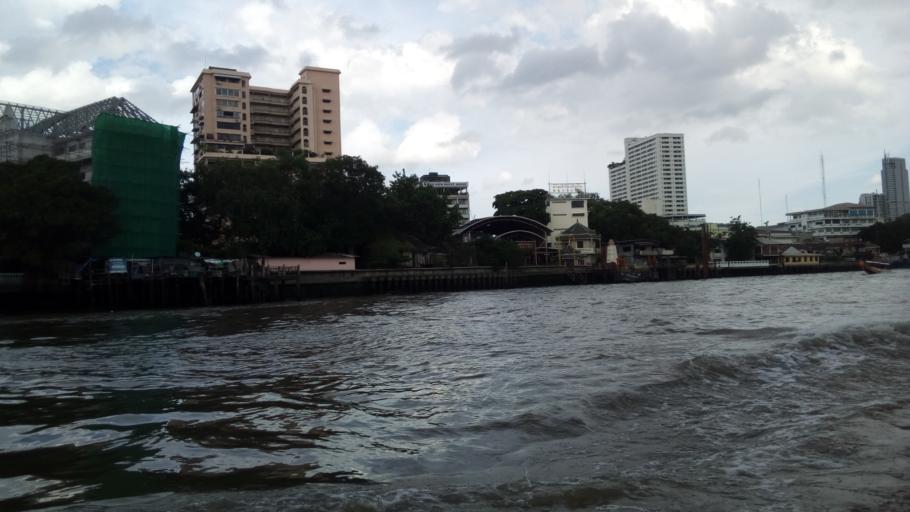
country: TH
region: Bangkok
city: Khlong San
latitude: 13.7349
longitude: 100.5101
